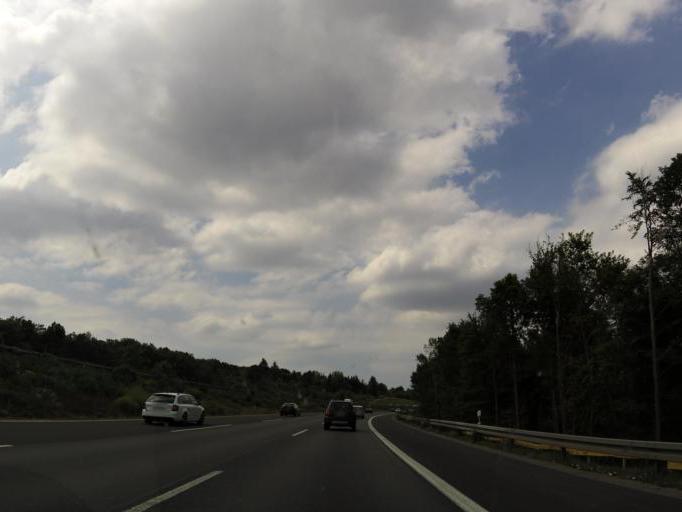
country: DE
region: Bavaria
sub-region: Regierungsbezirk Unterfranken
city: Randersacker
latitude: 49.7411
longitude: 9.9711
